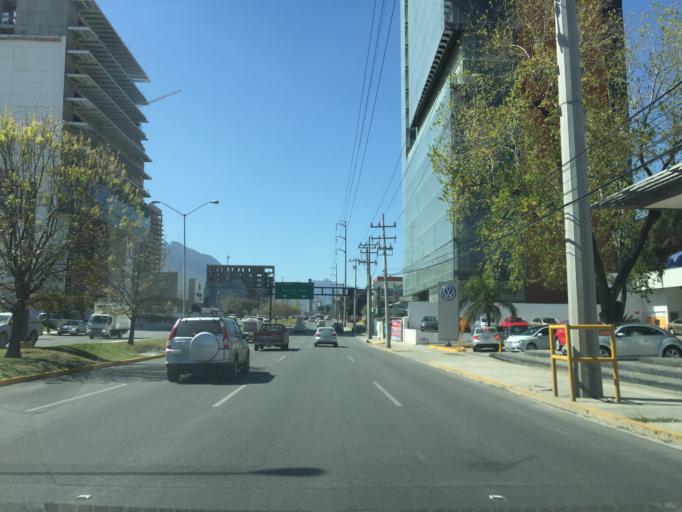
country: MX
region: Nuevo Leon
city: Garza Garcia
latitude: 25.6534
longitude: -100.3474
